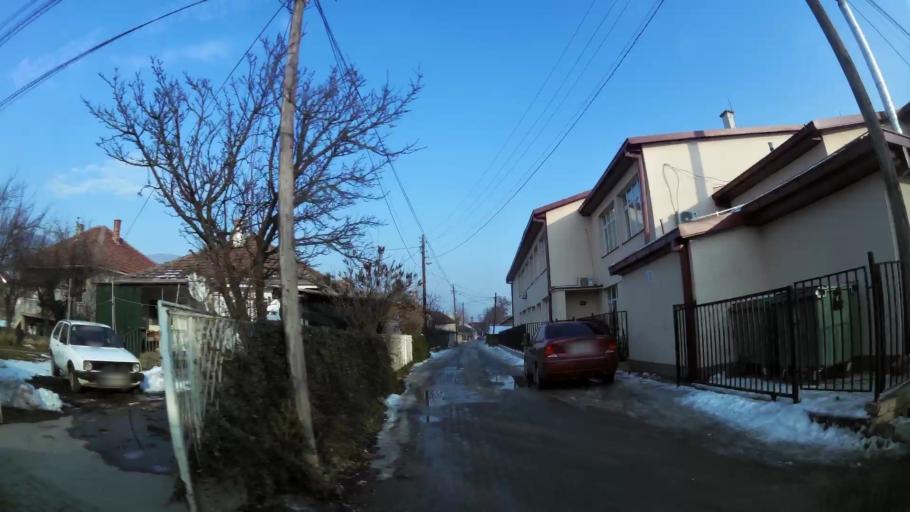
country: MK
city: Creshevo
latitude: 42.0281
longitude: 21.5130
